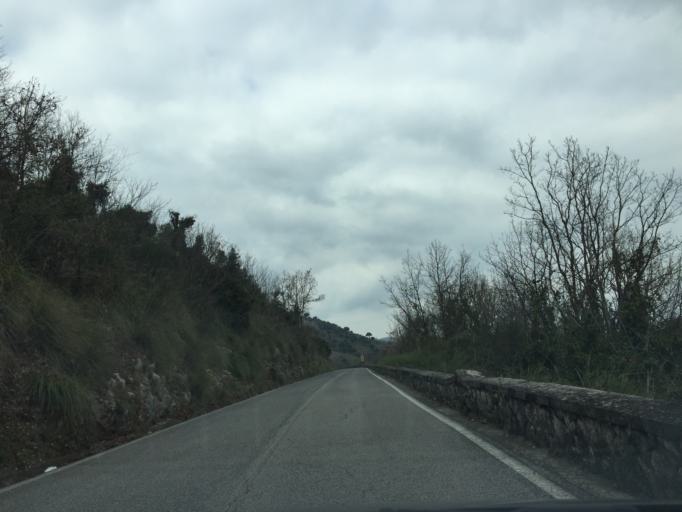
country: IT
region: Latium
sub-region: Provincia di Frosinone
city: Cassino
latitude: 41.4913
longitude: 13.8207
